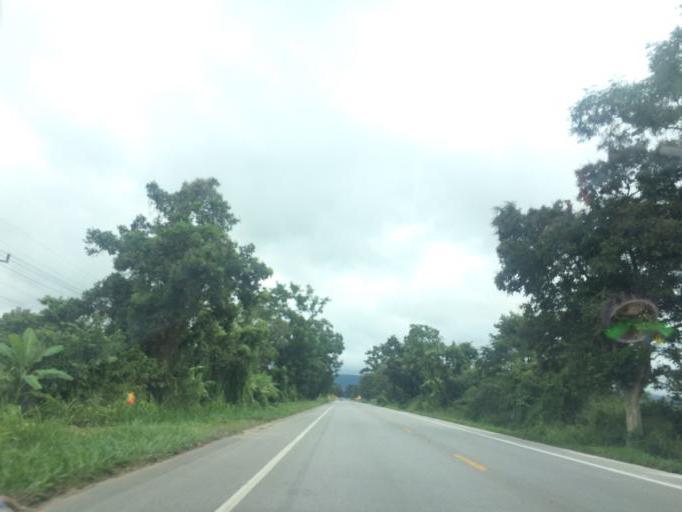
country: TH
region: Chiang Rai
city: Mae Lao
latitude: 19.7462
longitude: 99.6996
